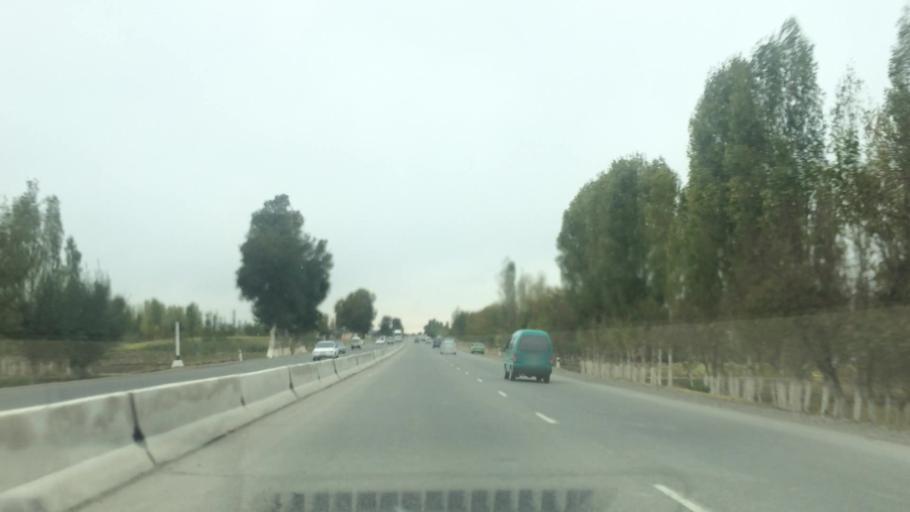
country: UZ
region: Samarqand
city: Jomboy
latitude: 39.7305
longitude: 67.1544
